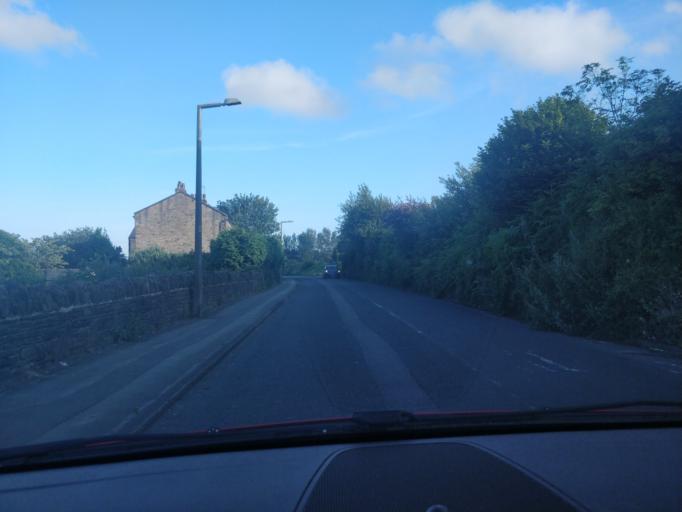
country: GB
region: England
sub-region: Lancashire
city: Appley Bridge
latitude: 53.5371
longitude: -2.7213
